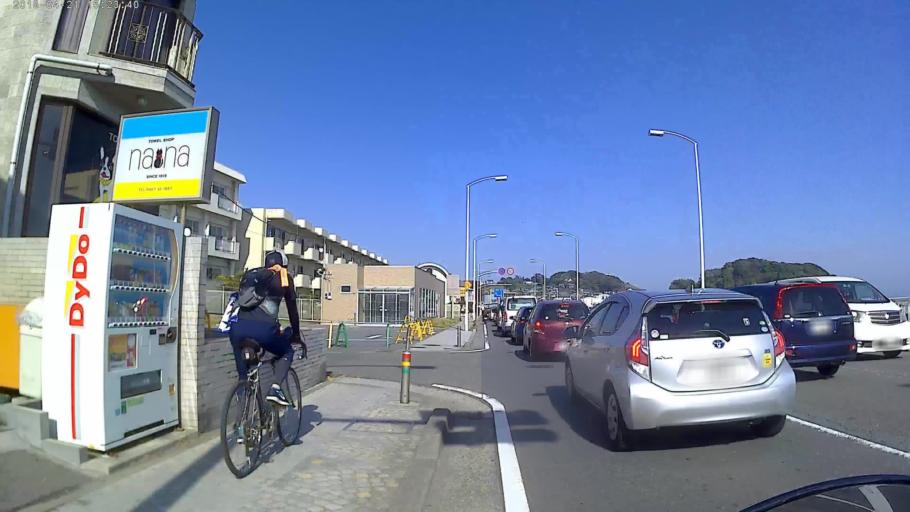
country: JP
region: Kanagawa
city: Fujisawa
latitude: 35.3084
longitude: 139.4891
